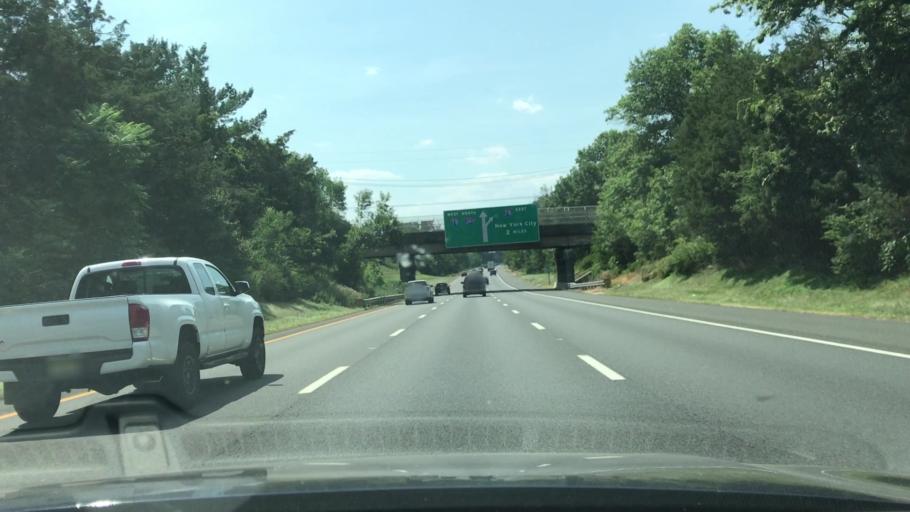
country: US
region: New Jersey
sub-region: Somerset County
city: Somerville
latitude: 40.5819
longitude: -74.5966
